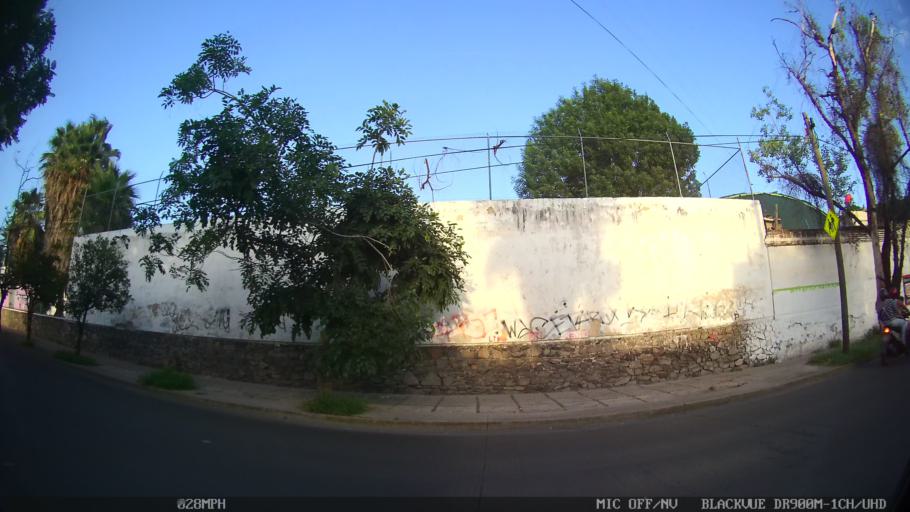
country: MX
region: Jalisco
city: Tlaquepaque
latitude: 20.6711
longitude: -103.3142
